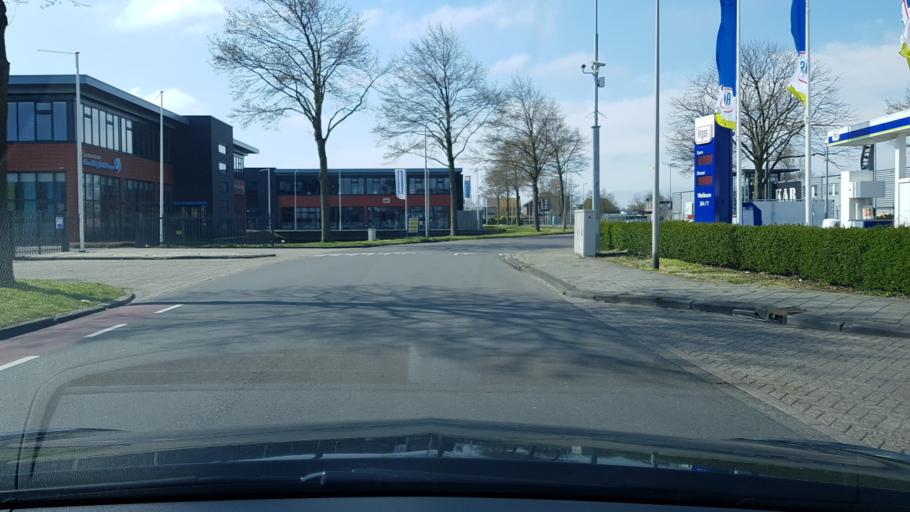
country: NL
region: South Holland
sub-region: Gemeente Noordwijkerhout
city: Noordwijkerhout
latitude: 52.2482
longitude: 4.4948
